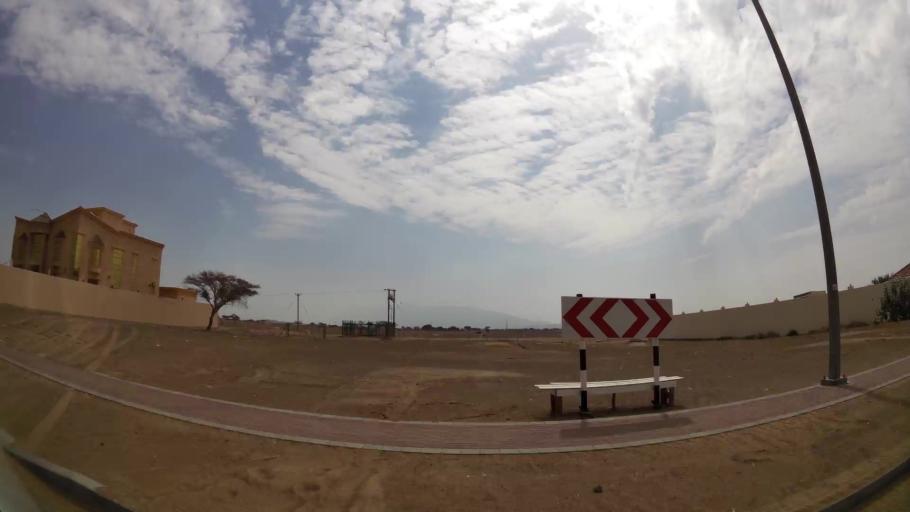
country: AE
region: Abu Dhabi
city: Al Ain
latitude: 24.1857
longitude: 55.8042
